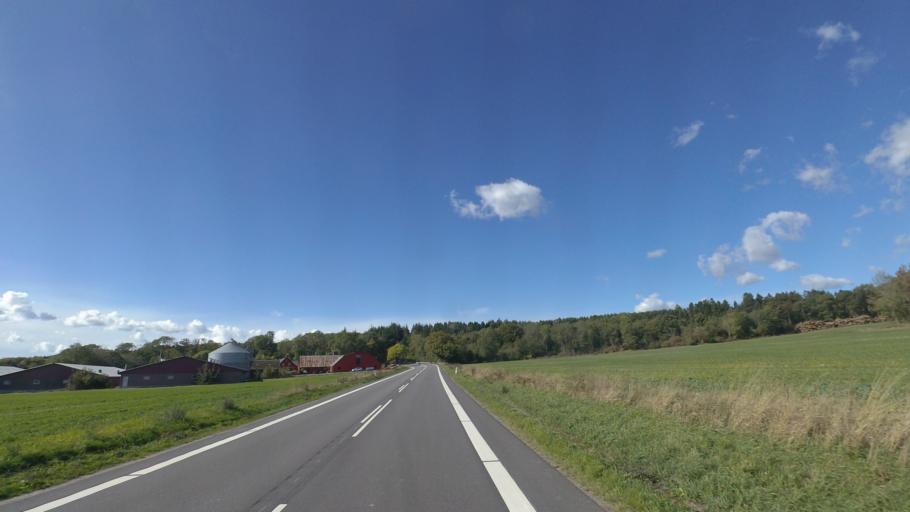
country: DK
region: Capital Region
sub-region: Bornholm Kommune
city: Akirkeby
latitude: 55.0639
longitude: 15.0229
